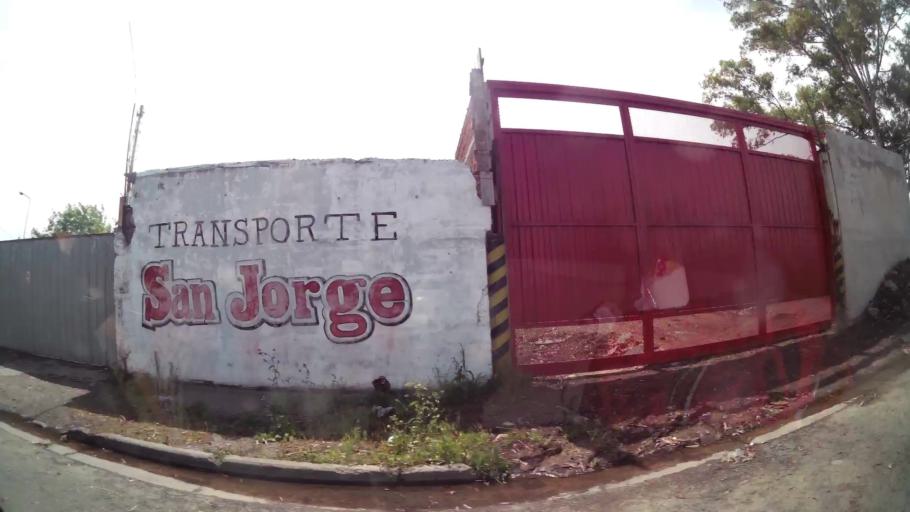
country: AR
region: Buenos Aires F.D.
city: Villa Lugano
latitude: -34.6684
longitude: -58.4331
